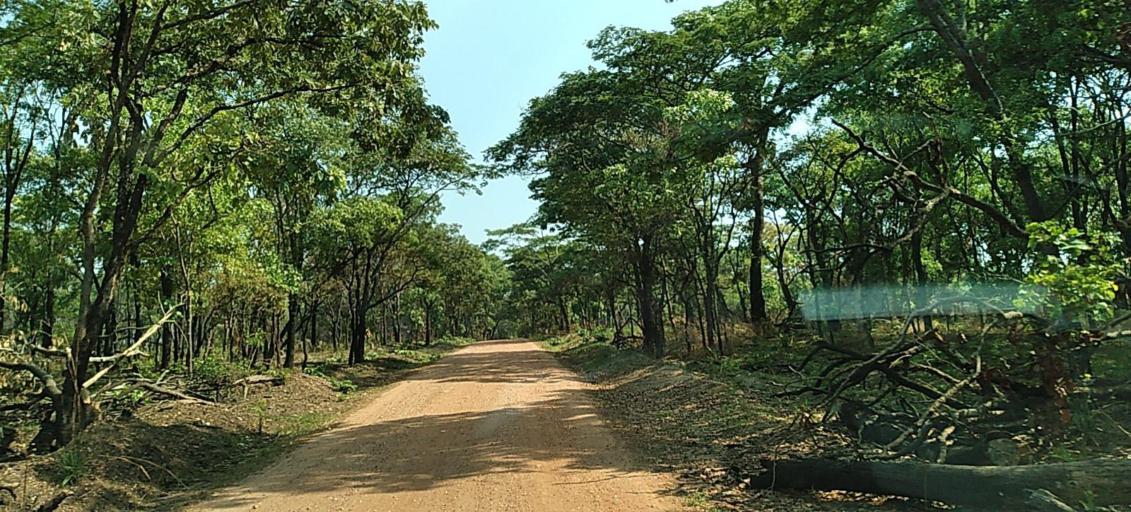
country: ZM
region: Copperbelt
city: Kalulushi
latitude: -12.9322
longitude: 27.8215
